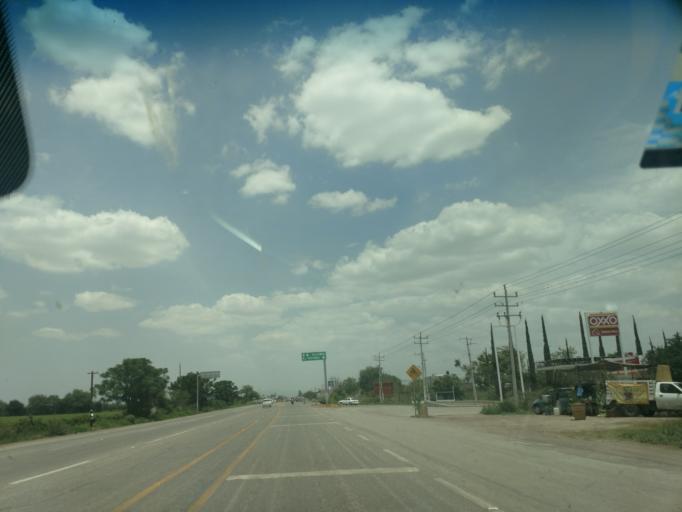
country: MX
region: San Luis Potosi
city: Ciudad Fernandez
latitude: 21.9421
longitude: -100.0425
